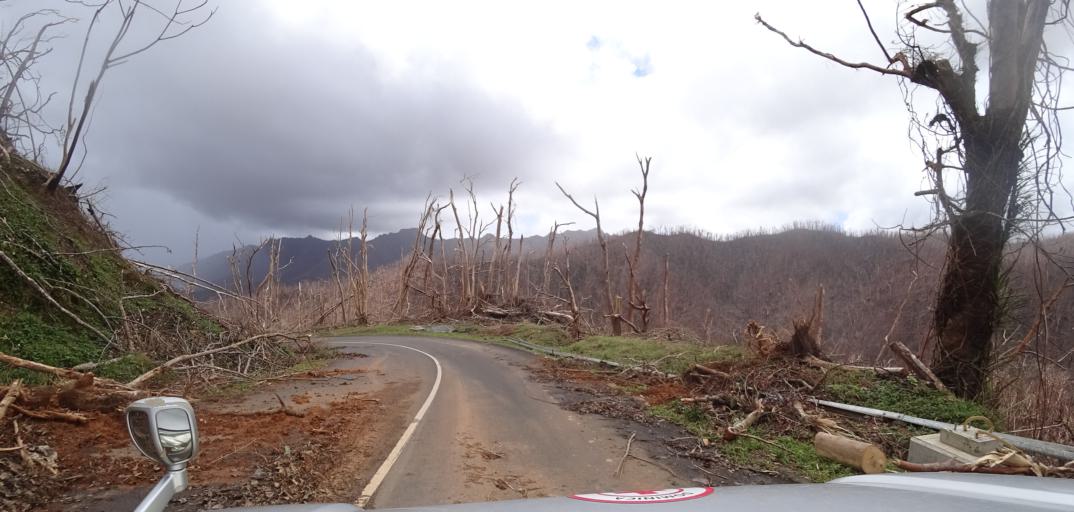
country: DM
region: Saint David
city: Castle Bruce
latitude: 15.4662
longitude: -61.3066
